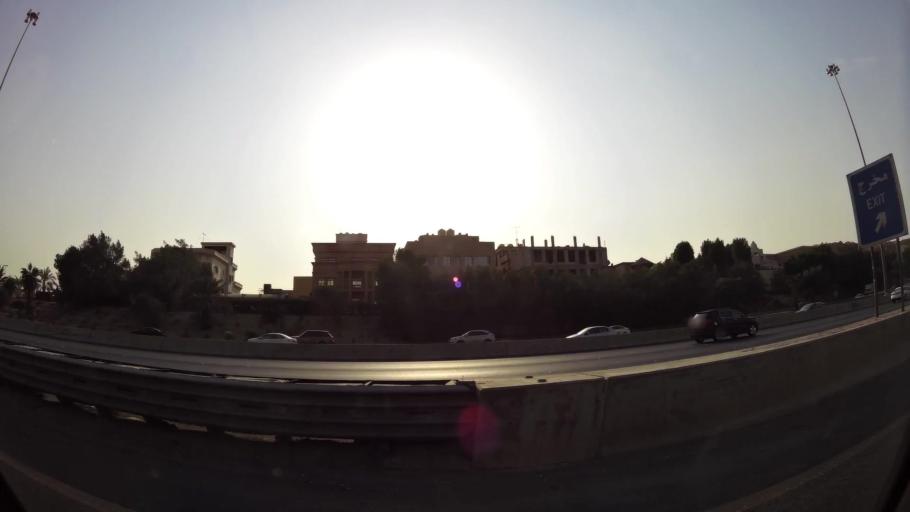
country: KW
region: Muhafazat Hawalli
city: Hawalli
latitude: 29.3204
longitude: 48.0144
